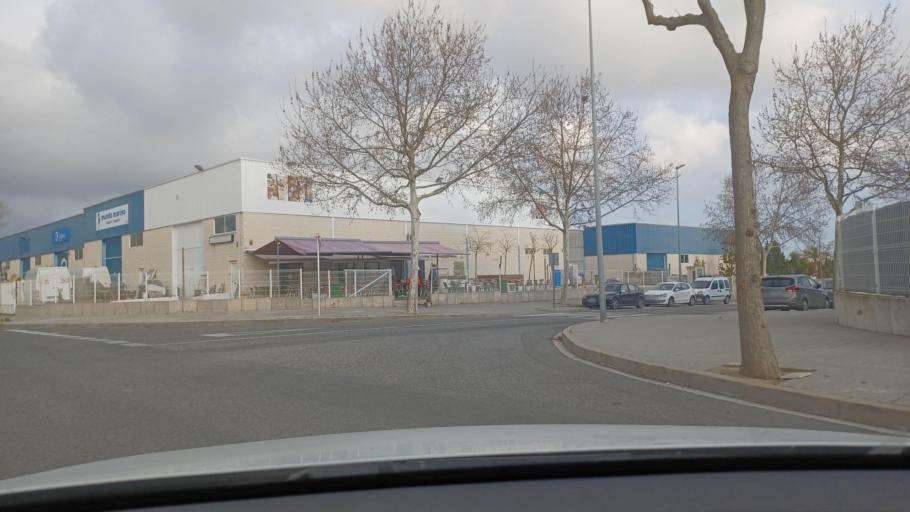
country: ES
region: Catalonia
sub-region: Provincia de Tarragona
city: Vila-seca
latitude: 41.1191
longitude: 1.1497
